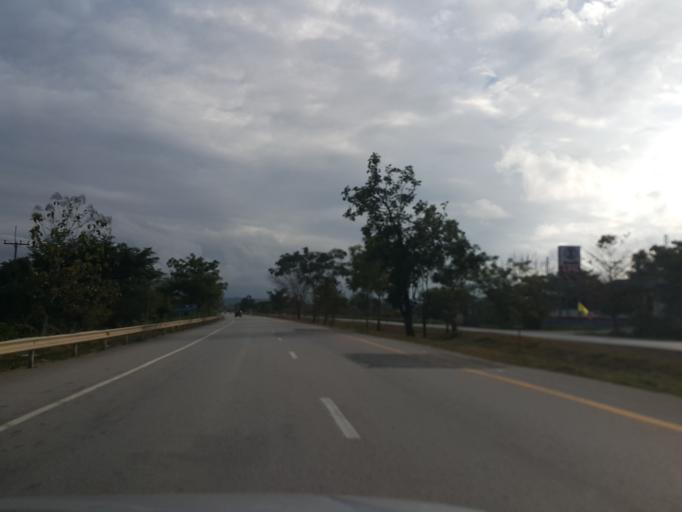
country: TH
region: Lampang
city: Ko Kha
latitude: 18.1587
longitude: 99.4036
